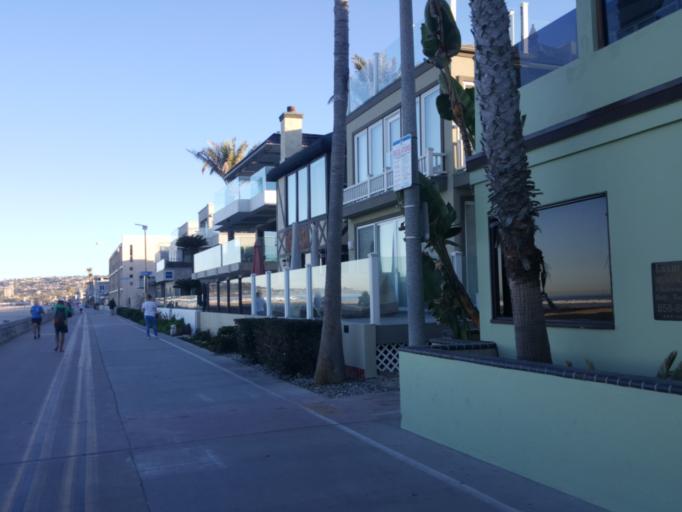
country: US
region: California
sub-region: San Diego County
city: La Jolla
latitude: 32.7827
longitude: -117.2536
